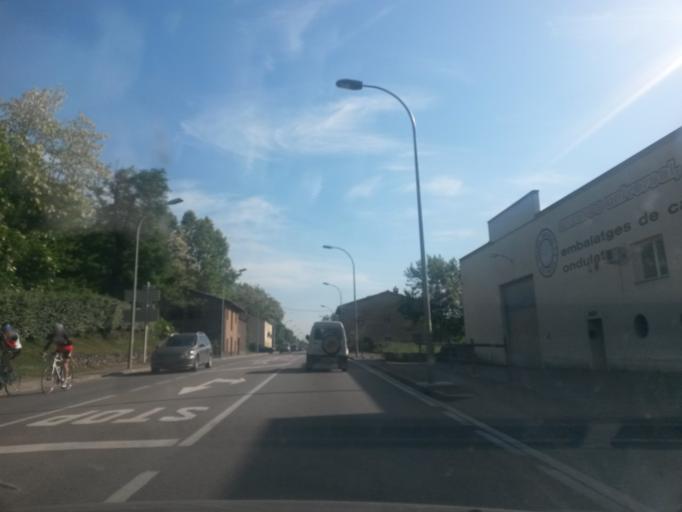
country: ES
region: Catalonia
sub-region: Provincia de Girona
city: Olot
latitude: 42.1580
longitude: 2.4665
